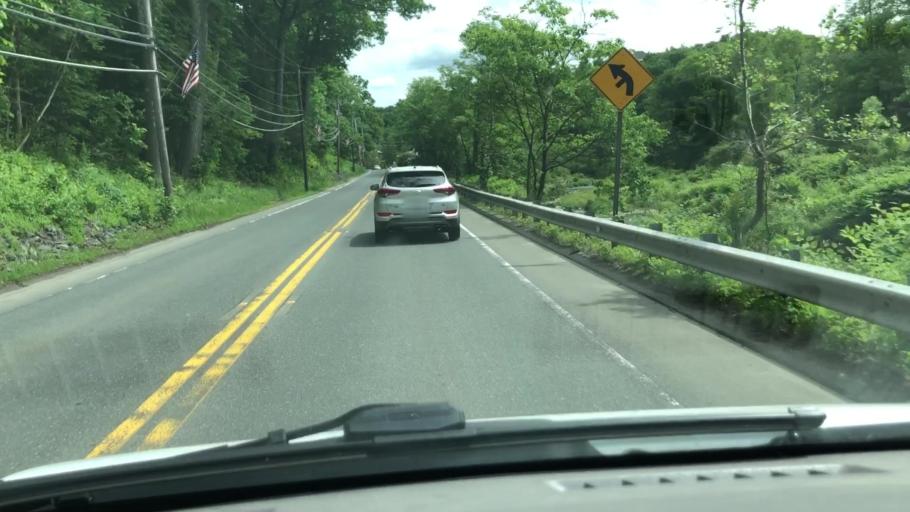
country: US
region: Massachusetts
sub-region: Hampshire County
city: Williamsburg
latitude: 42.3793
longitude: -72.7066
